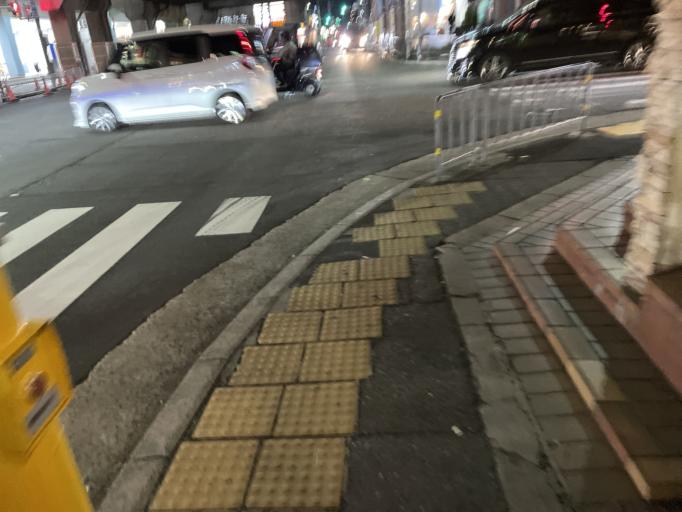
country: JP
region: Osaka
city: Yao
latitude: 34.6642
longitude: 135.5889
